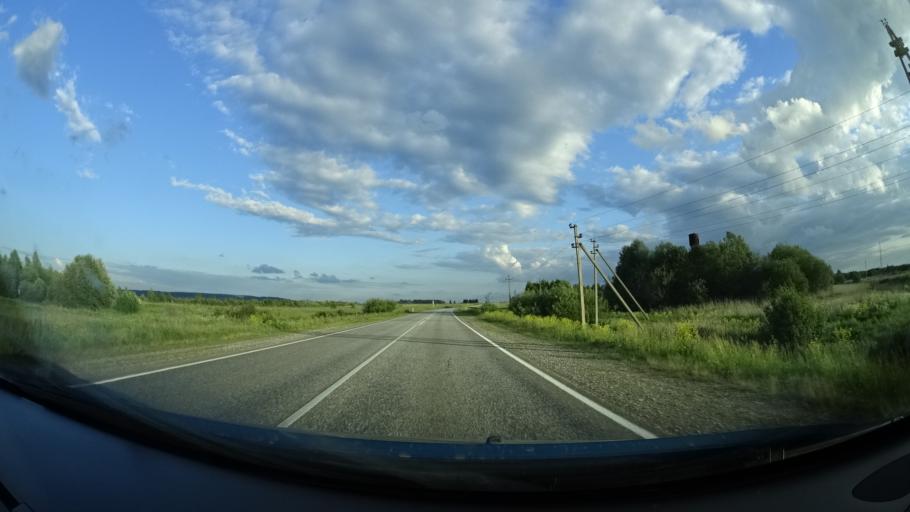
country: RU
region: Perm
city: Barda
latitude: 57.0829
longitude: 55.5422
